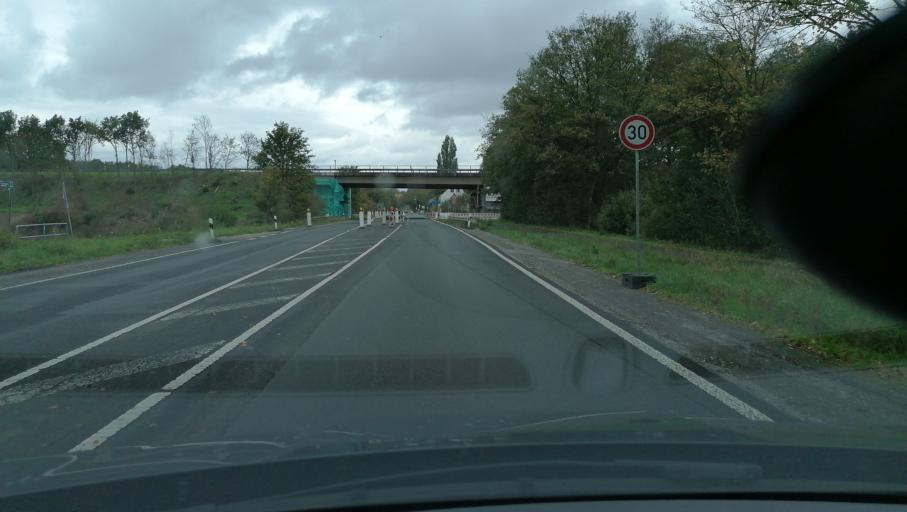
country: DE
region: North Rhine-Westphalia
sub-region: Regierungsbezirk Munster
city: Recklinghausen
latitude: 51.6509
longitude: 7.1858
